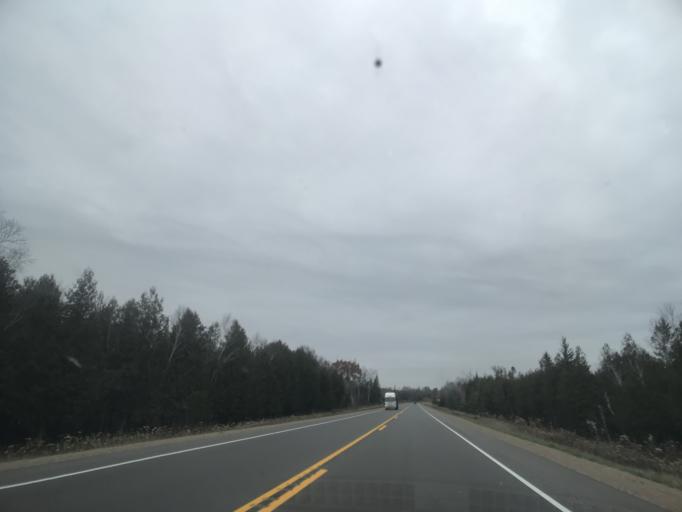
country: US
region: Wisconsin
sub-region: Menominee County
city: Legend Lake
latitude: 45.2592
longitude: -88.5137
